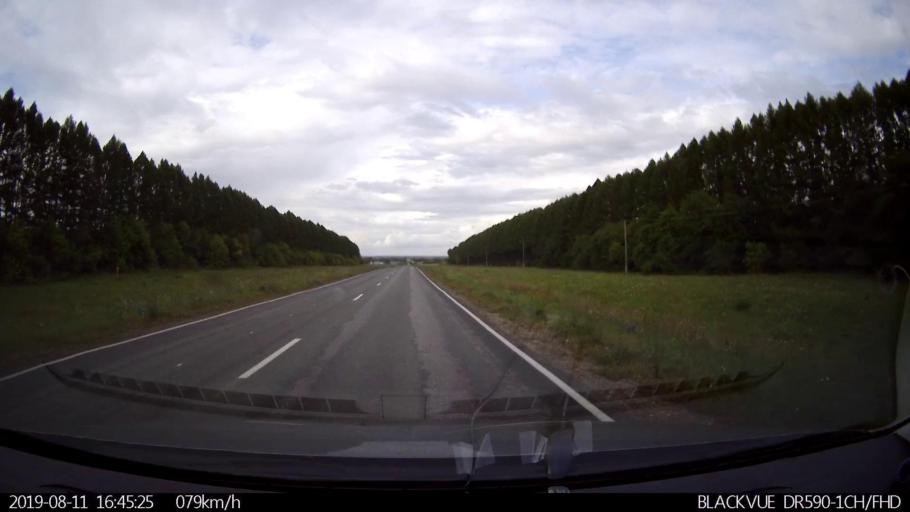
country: RU
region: Ulyanovsk
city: Mayna
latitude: 54.1896
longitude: 47.6859
